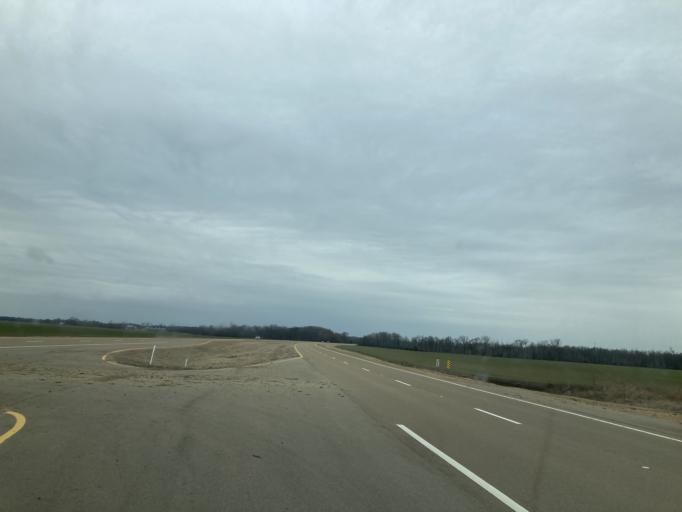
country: US
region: Mississippi
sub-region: Yazoo County
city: Yazoo City
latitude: 32.9814
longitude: -90.4610
